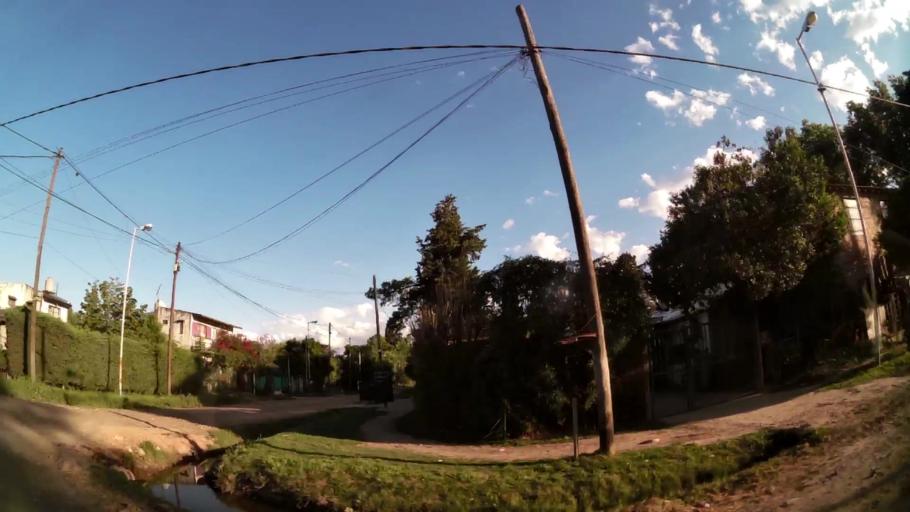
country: AR
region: Buenos Aires
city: Santa Catalina - Dique Lujan
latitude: -34.4701
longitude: -58.7473
